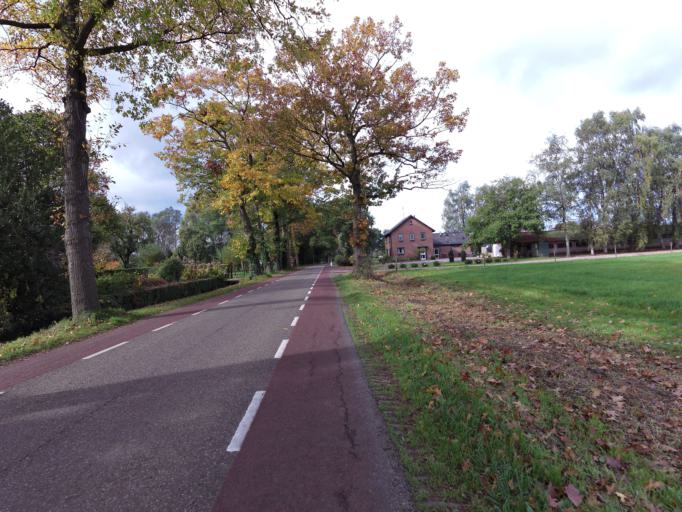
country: NL
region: Gelderland
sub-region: Gemeente Bronckhorst
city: Hengelo
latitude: 52.0711
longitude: 6.2845
